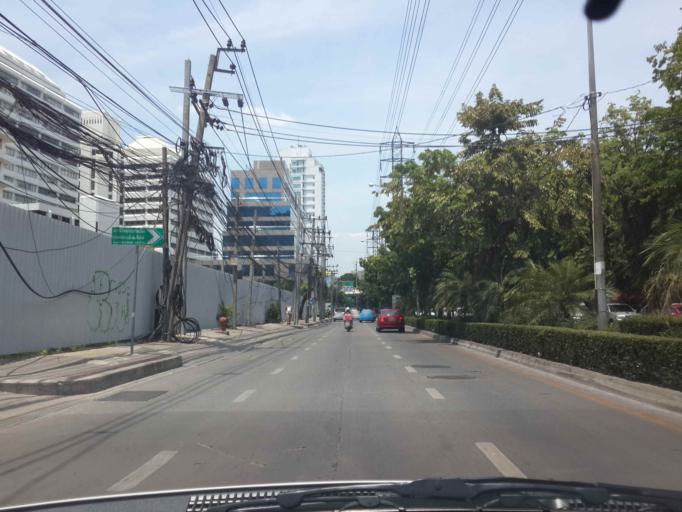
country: TH
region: Bangkok
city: Pathum Wan
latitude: 13.7342
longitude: 100.5438
